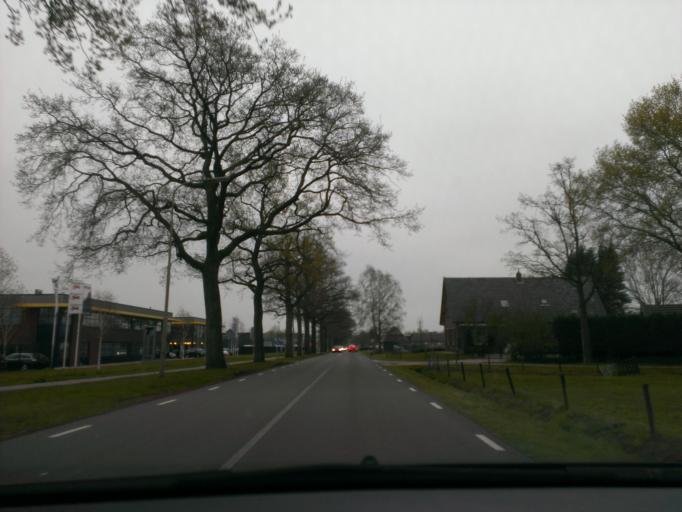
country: NL
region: Gelderland
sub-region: Gemeente Epe
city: Emst
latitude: 52.2977
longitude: 5.9862
